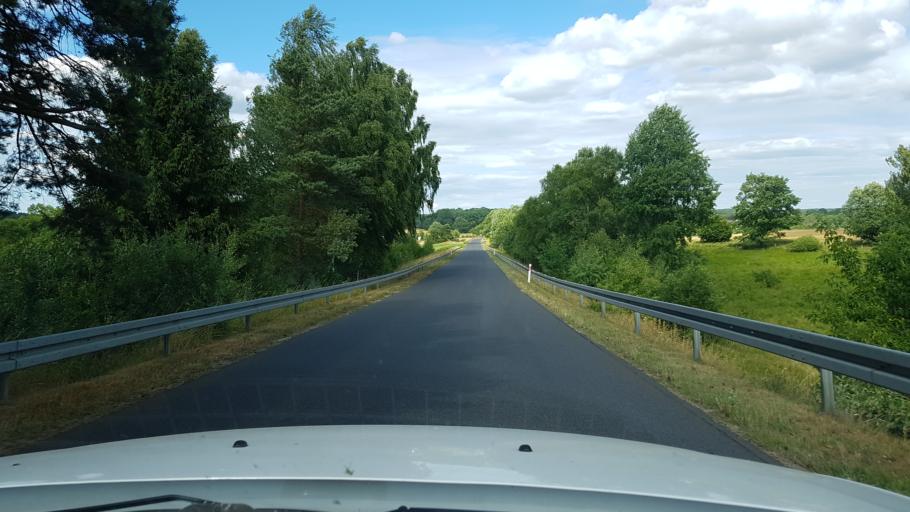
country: PL
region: West Pomeranian Voivodeship
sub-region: Powiat drawski
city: Kalisz Pomorski
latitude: 53.3960
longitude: 15.9611
